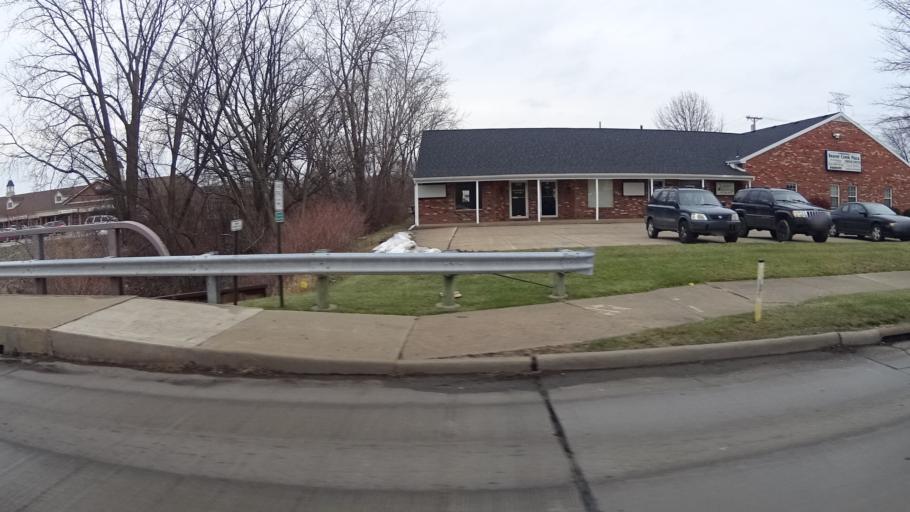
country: US
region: Ohio
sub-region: Lorain County
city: Amherst
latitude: 41.4167
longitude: -82.2063
